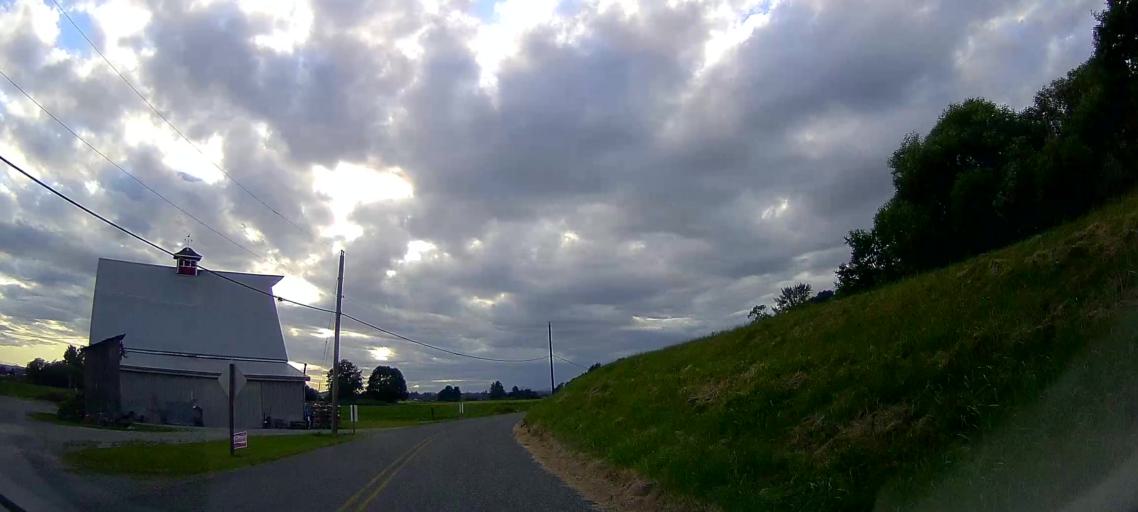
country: US
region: Washington
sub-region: Skagit County
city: Mount Vernon
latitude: 48.3427
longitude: -122.3540
